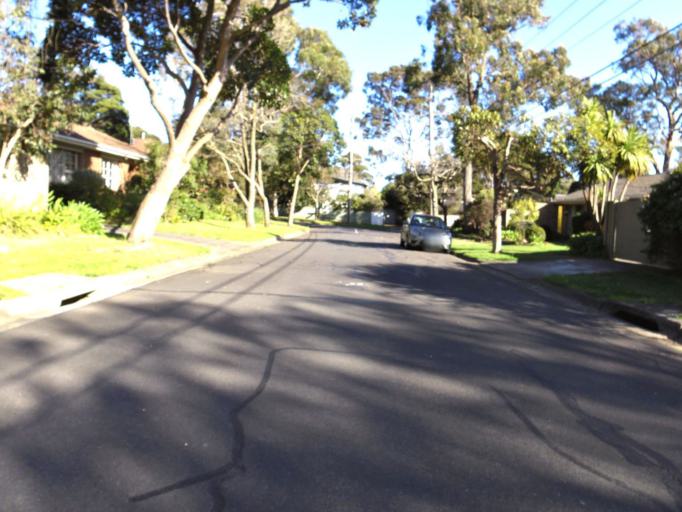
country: AU
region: Victoria
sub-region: Maroondah
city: Heathmont
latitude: -37.8337
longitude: 145.2332
